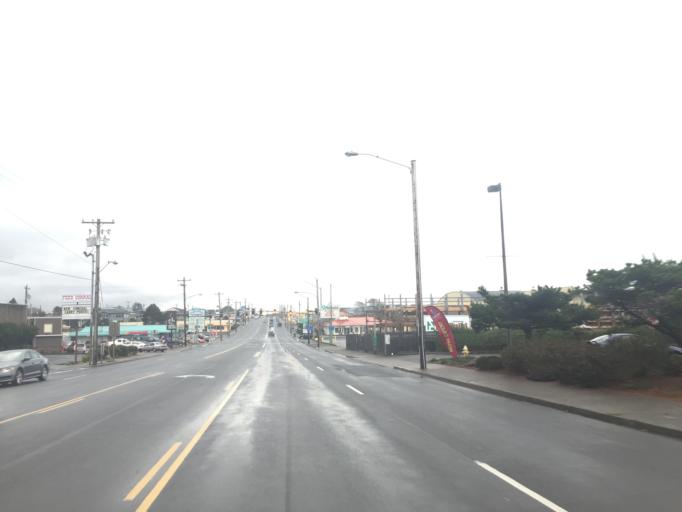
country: US
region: Oregon
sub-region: Lincoln County
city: Newport
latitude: 44.6415
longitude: -124.0531
